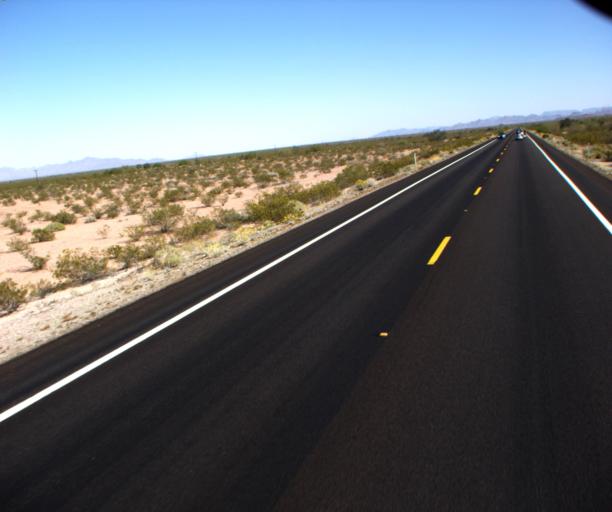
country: US
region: Arizona
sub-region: La Paz County
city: Quartzsite
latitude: 33.2904
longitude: -114.2258
